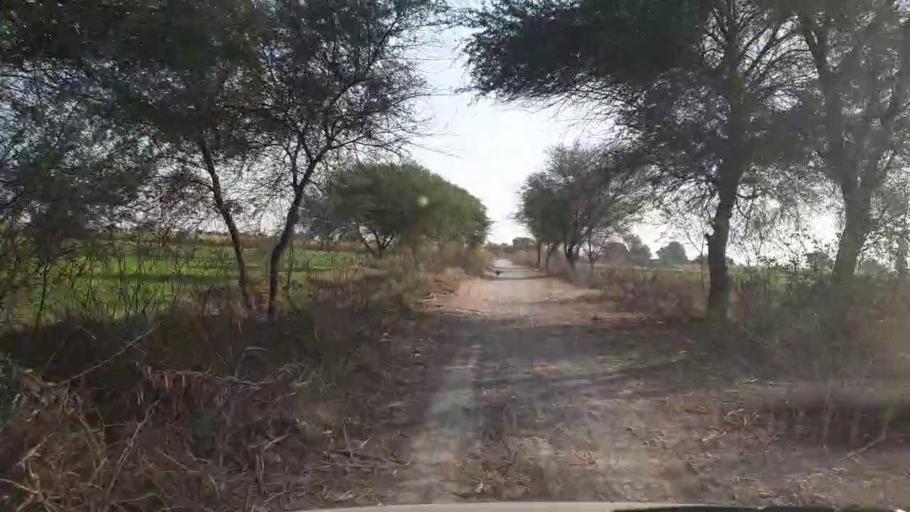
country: PK
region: Sindh
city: Chambar
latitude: 25.3165
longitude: 68.7637
